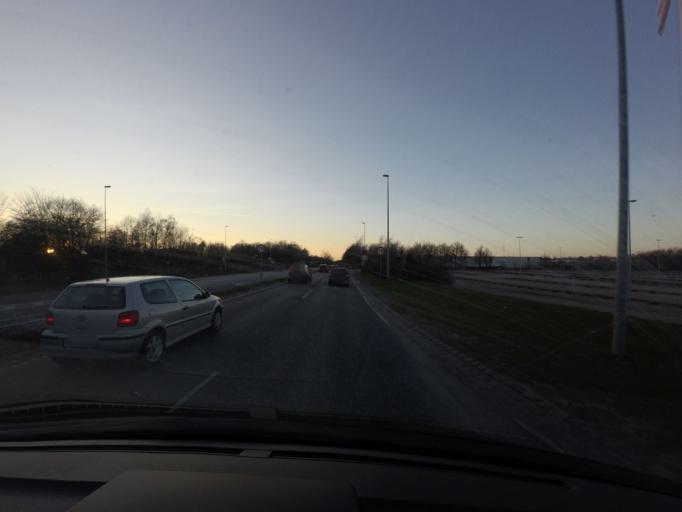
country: DK
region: South Denmark
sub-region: Odense Kommune
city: Neder Holluf
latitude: 55.3720
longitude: 10.4454
